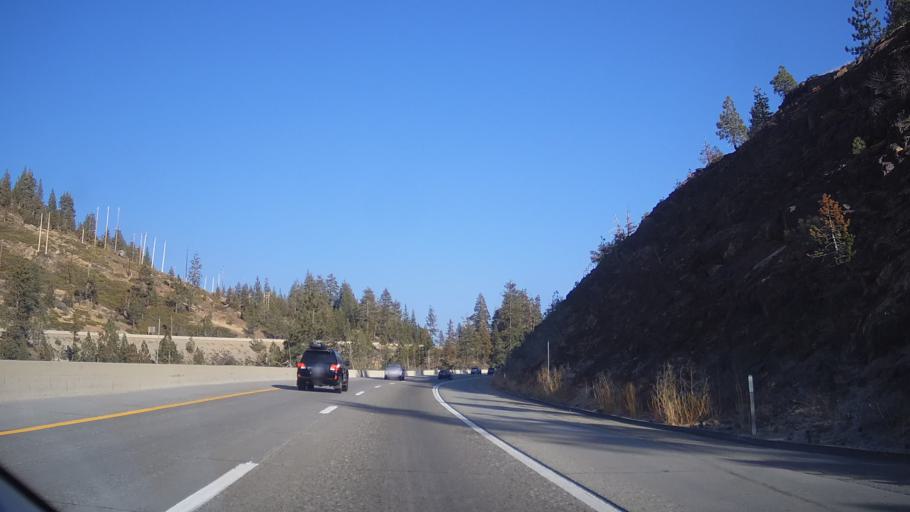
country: US
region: California
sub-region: Nevada County
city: Truckee
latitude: 39.3049
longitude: -120.5289
